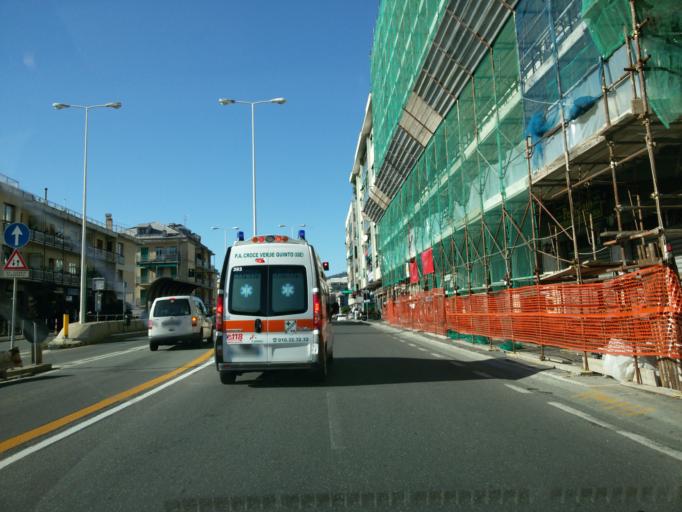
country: IT
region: Liguria
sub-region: Provincia di Genova
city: Genoa
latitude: 44.3993
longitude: 8.9897
